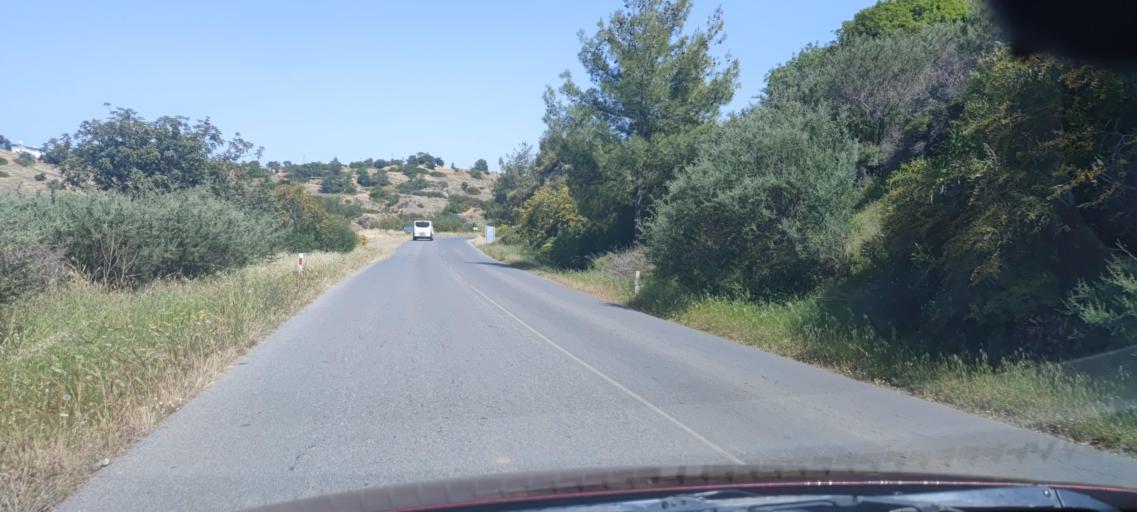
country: CY
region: Lefkosia
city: Kato Pyrgos
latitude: 35.1577
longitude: 32.7567
